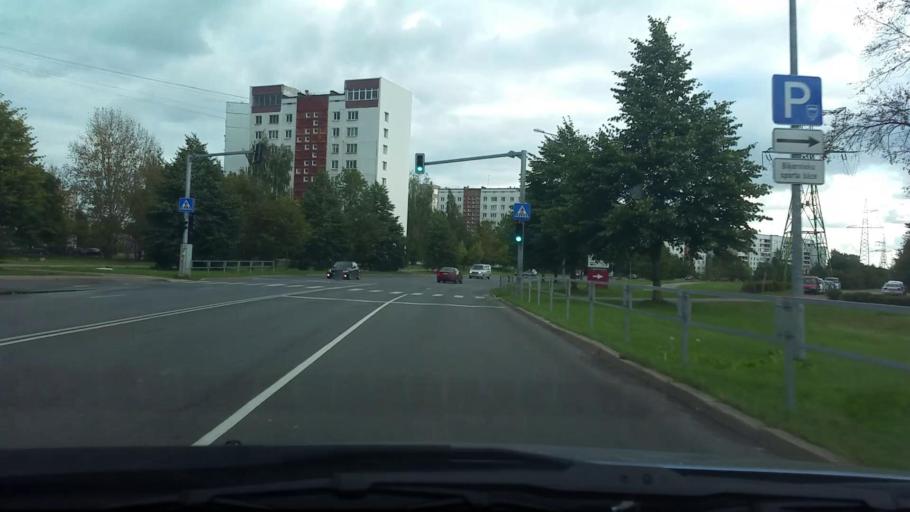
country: LV
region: Stopini
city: Ulbroka
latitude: 56.9659
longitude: 24.2334
